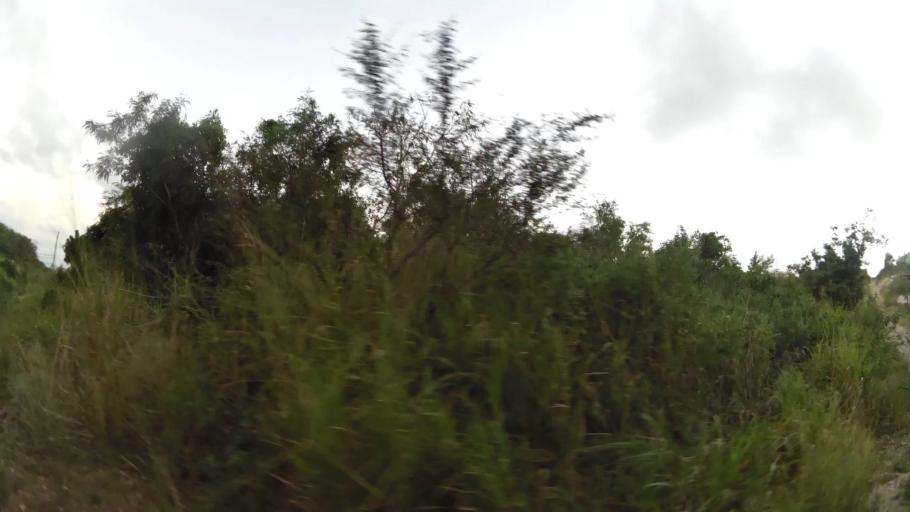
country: AG
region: Saint George
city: Piggotts
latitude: 17.1366
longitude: -61.8043
